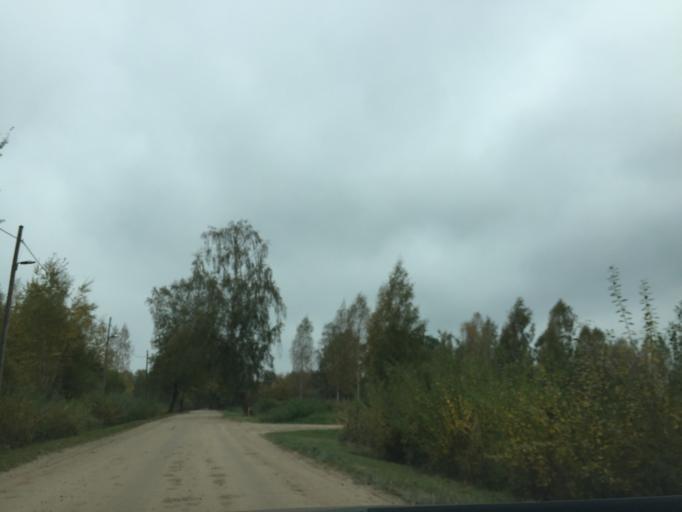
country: LV
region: Jelgava
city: Jelgava
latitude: 56.6855
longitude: 23.7408
